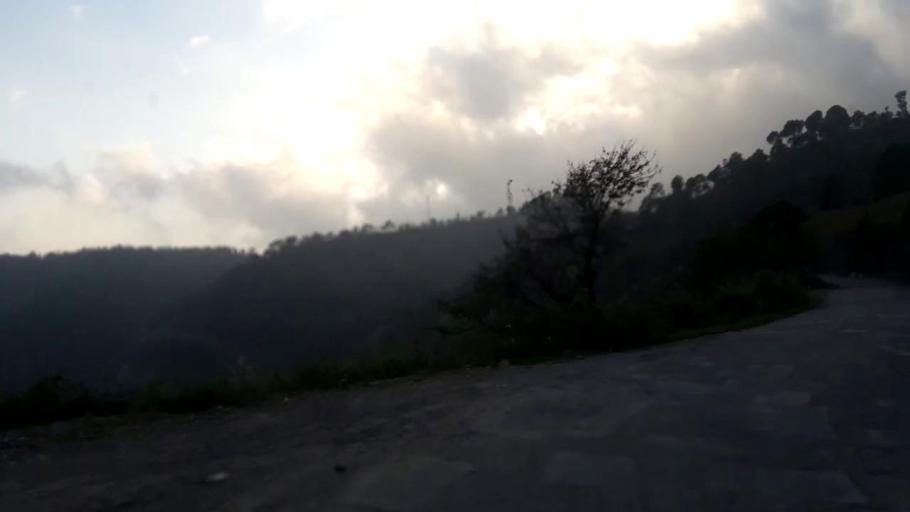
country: IN
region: Himachal Pradesh
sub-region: Shimla
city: Shimla
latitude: 31.0528
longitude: 77.1579
